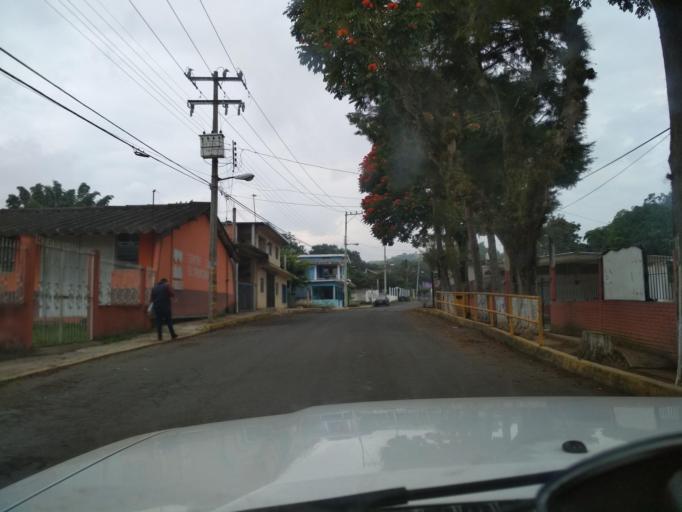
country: MX
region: Veracruz
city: El Castillo
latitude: 19.5648
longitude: -96.8651
